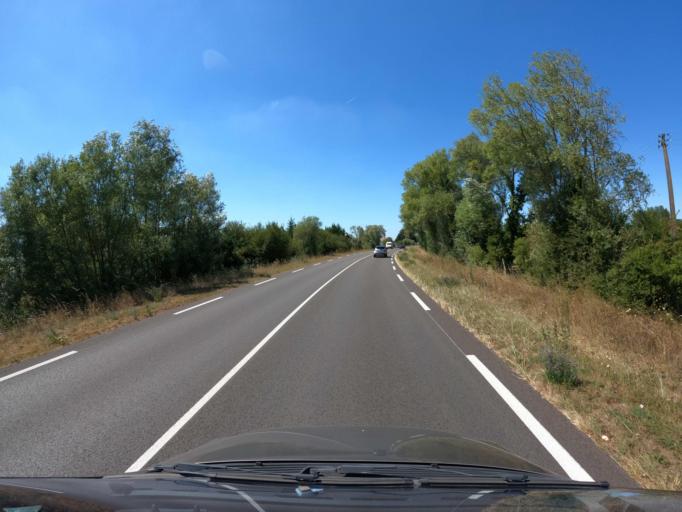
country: FR
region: Pays de la Loire
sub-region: Departement de la Vendee
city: Saint-Jean-de-Monts
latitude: 46.7971
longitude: -2.0497
